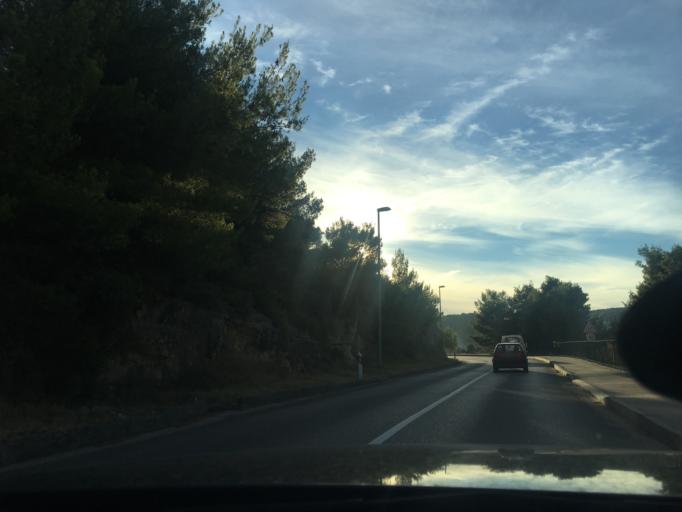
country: HR
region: Splitsko-Dalmatinska
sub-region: Grad Vis
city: Vis
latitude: 43.0561
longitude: 16.1960
